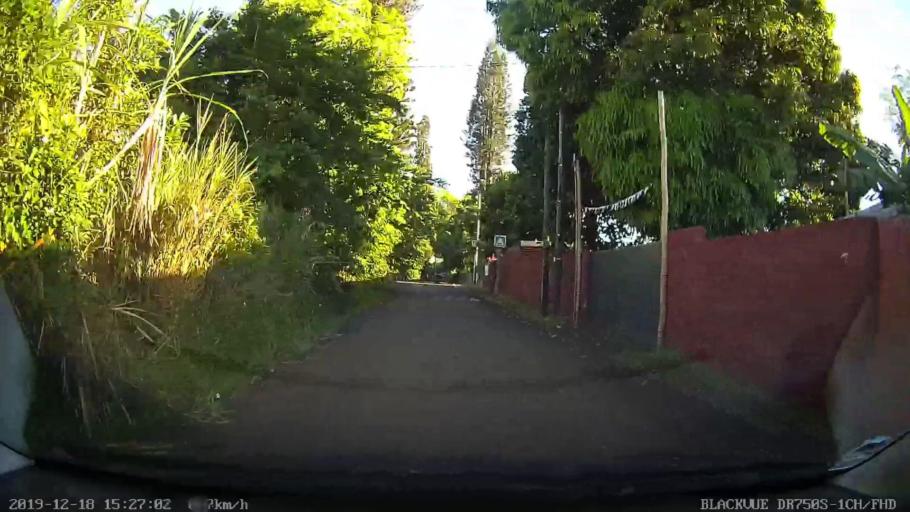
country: RE
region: Reunion
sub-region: Reunion
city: Bras-Panon
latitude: -21.0007
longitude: 55.6536
